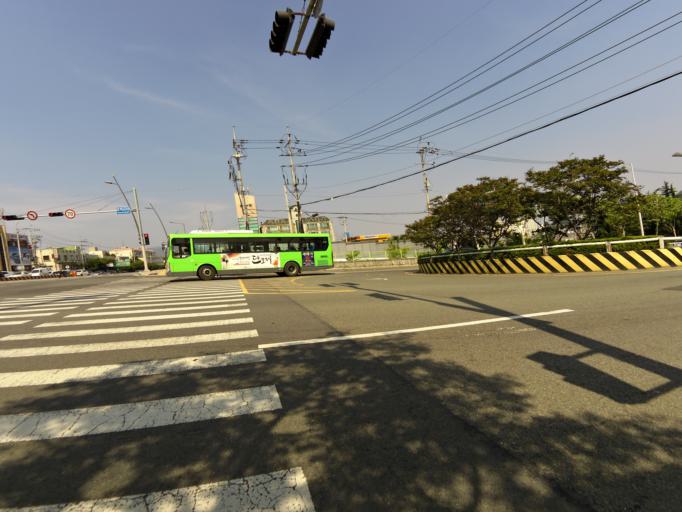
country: KR
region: Daegu
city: Daegu
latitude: 35.8763
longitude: 128.6450
